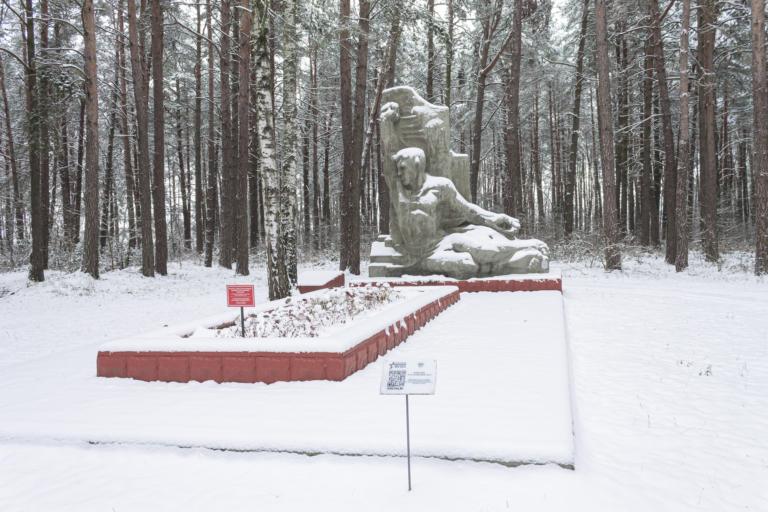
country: BY
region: Brest
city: Kamyanyets
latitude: 52.3863
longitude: 23.8550
